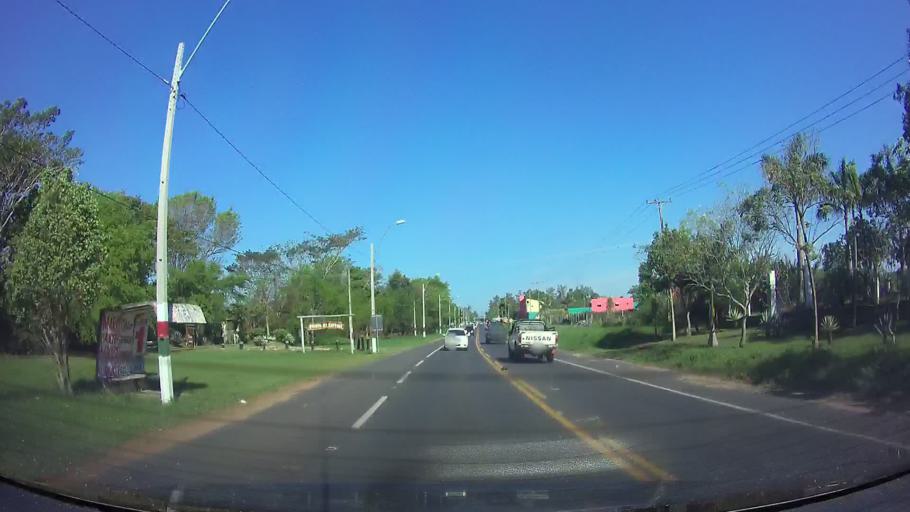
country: PY
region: Central
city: Aregua
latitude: -25.3263
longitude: -57.3623
